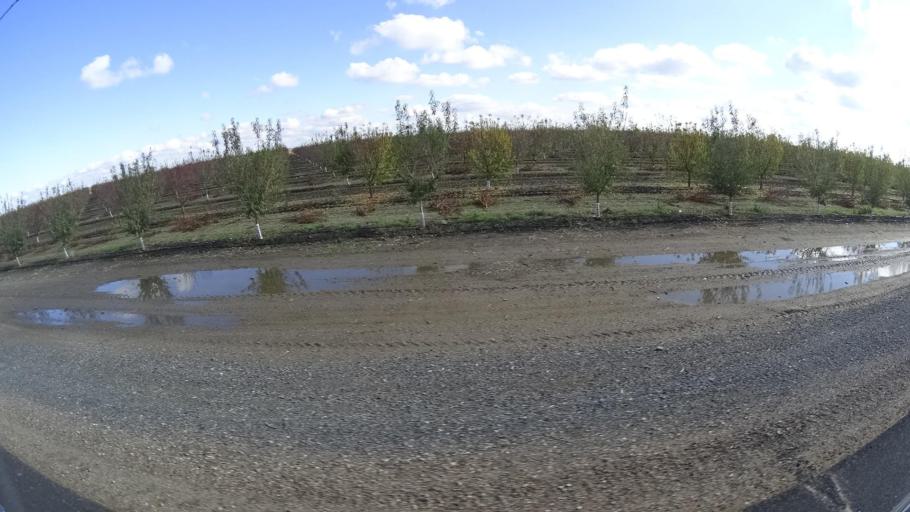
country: US
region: California
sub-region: Kern County
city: Wasco
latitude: 35.6703
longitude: -119.3307
